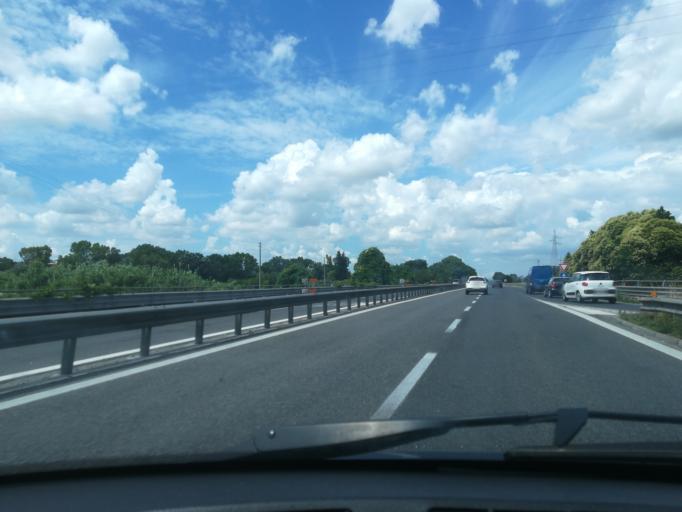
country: IT
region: The Marches
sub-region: Provincia di Macerata
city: Borgo Stazione
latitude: 43.2775
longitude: 13.6531
